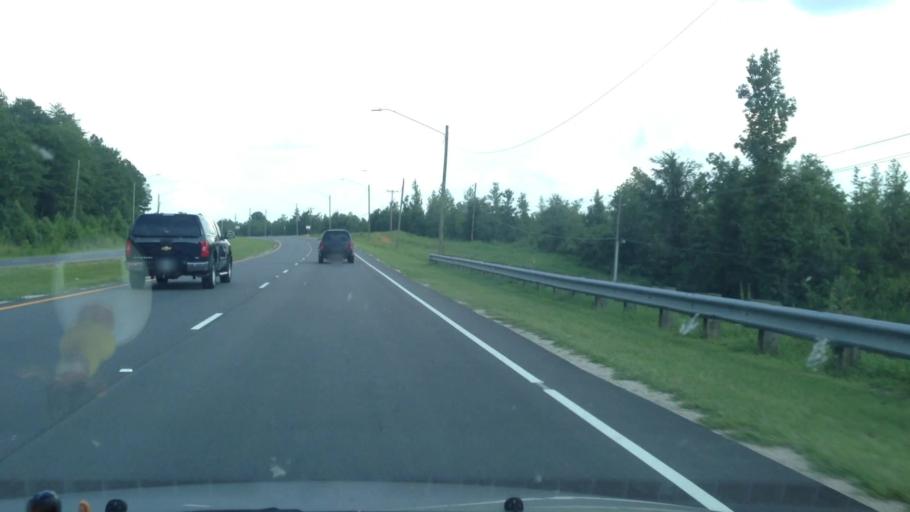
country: US
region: North Carolina
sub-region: Harnett County
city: Lillington
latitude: 35.4132
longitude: -78.7947
